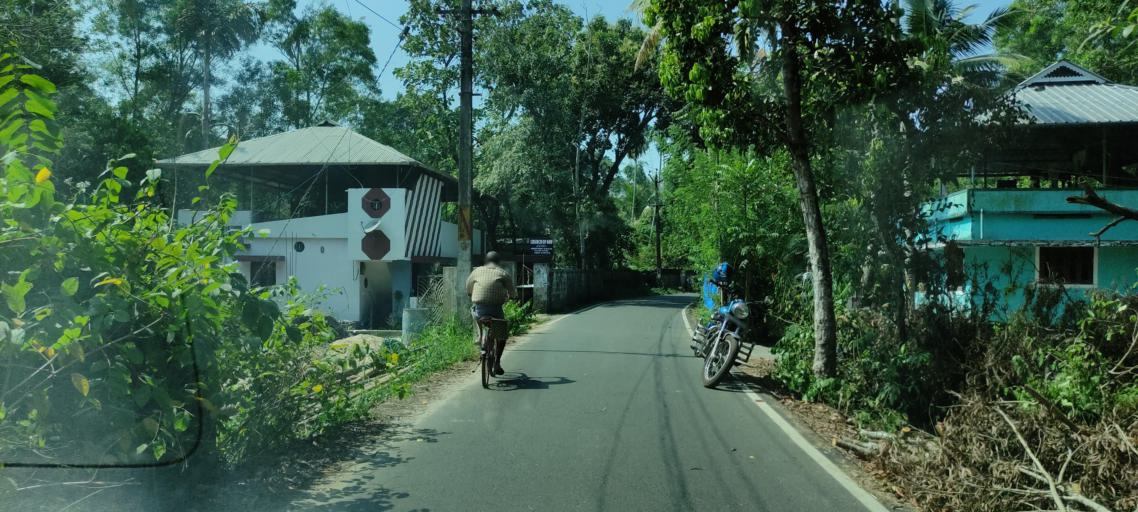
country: IN
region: Kerala
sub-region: Alappuzha
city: Alleppey
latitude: 9.5550
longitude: 76.3155
